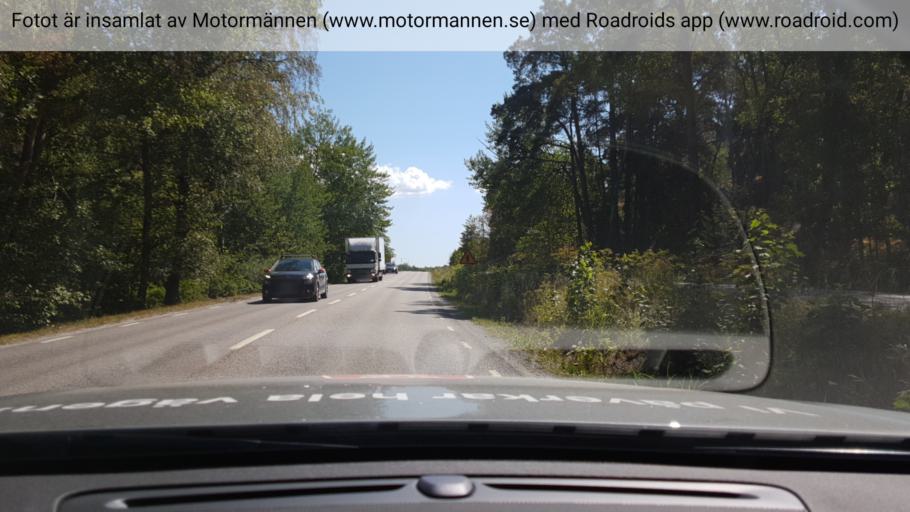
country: SE
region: Stockholm
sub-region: Ekero Kommun
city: Ekeroe
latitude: 59.3234
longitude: 17.7613
